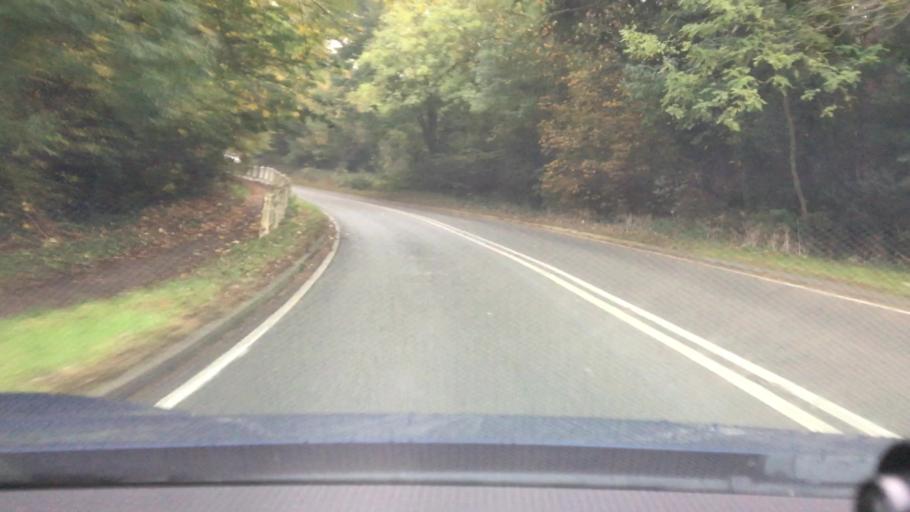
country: GB
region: England
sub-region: Leicestershire
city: Market Harborough
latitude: 52.4768
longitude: -0.9454
